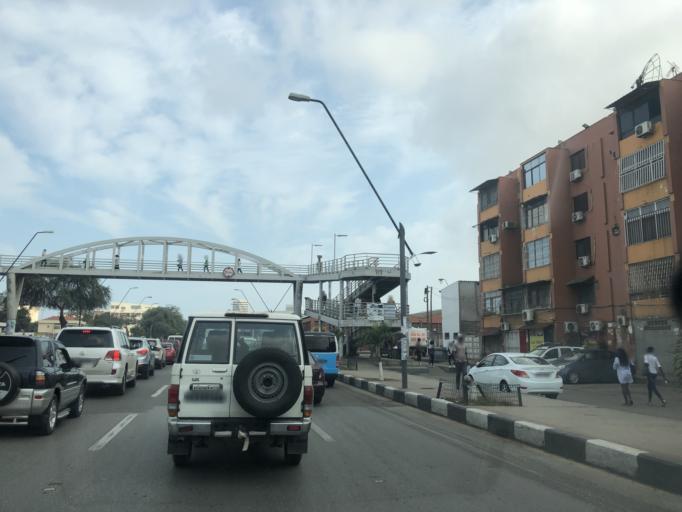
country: AO
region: Luanda
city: Luanda
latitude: -8.8438
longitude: 13.2333
